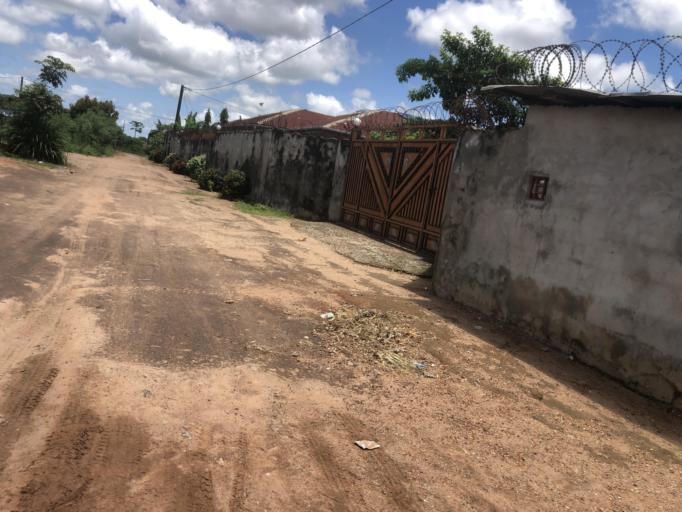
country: SL
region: Northern Province
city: Makeni
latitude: 8.8584
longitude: -12.0452
